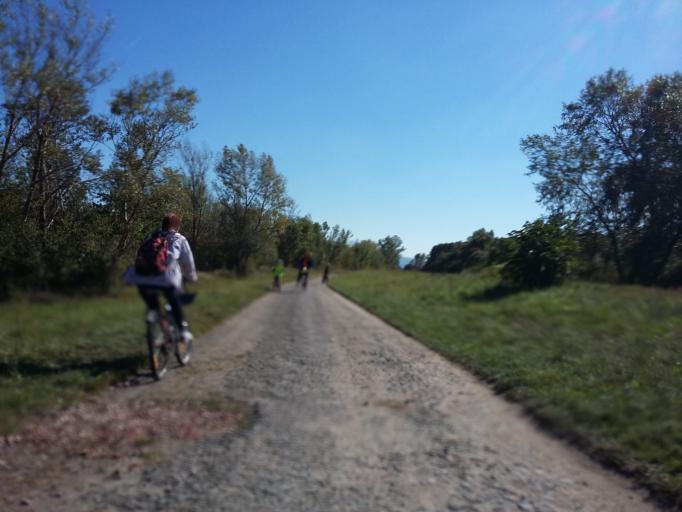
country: AT
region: Lower Austria
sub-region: Politischer Bezirk Ganserndorf
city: Marchegg
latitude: 48.3201
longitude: 16.9100
